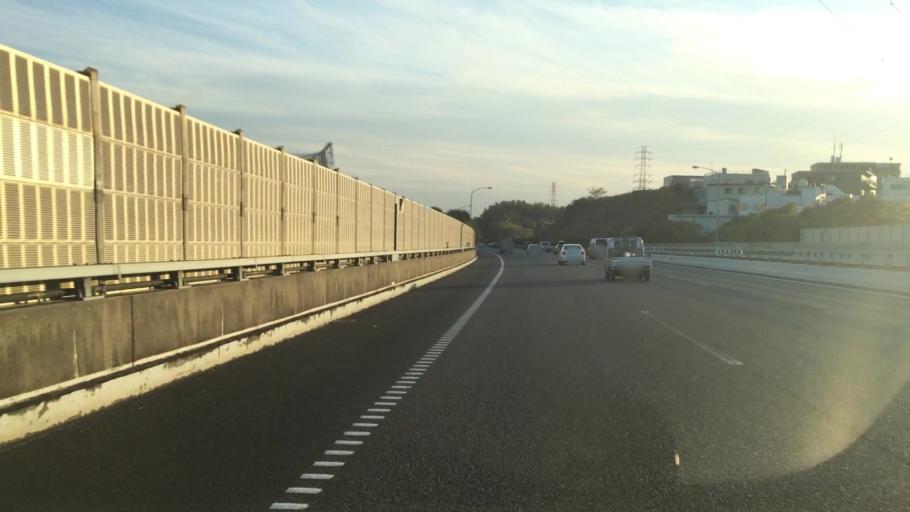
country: JP
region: Tokyo
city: Chofugaoka
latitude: 35.5635
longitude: 139.6101
